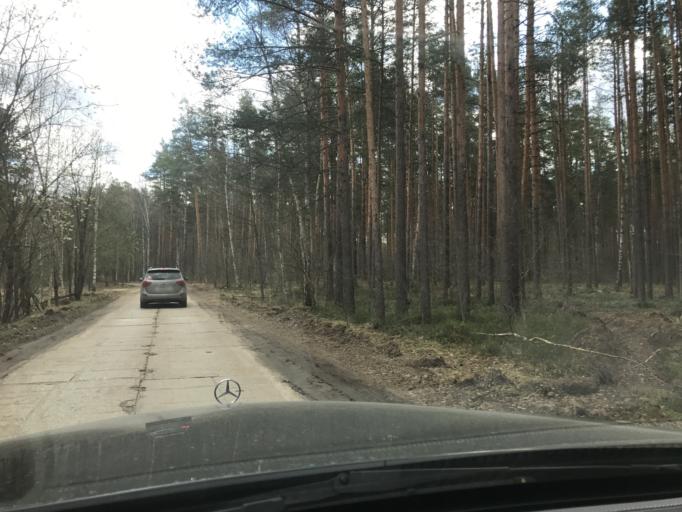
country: RU
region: Moskovskaya
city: Vereya
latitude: 55.8401
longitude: 39.1290
